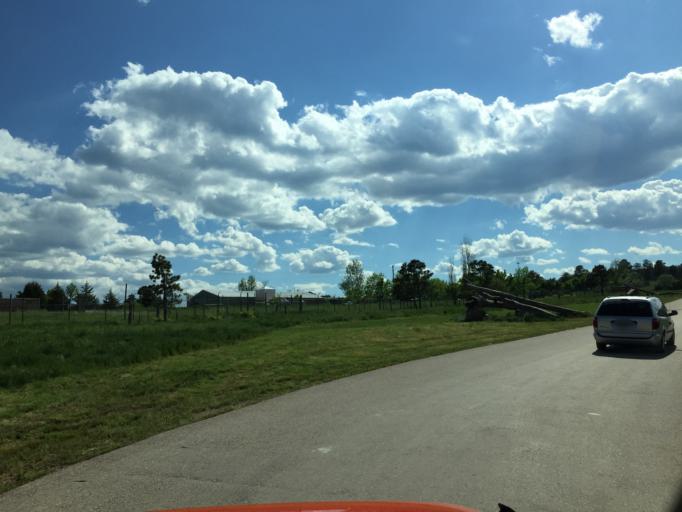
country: US
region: South Dakota
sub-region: Pennington County
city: Colonial Pine Hills
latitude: 43.9772
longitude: -103.2976
